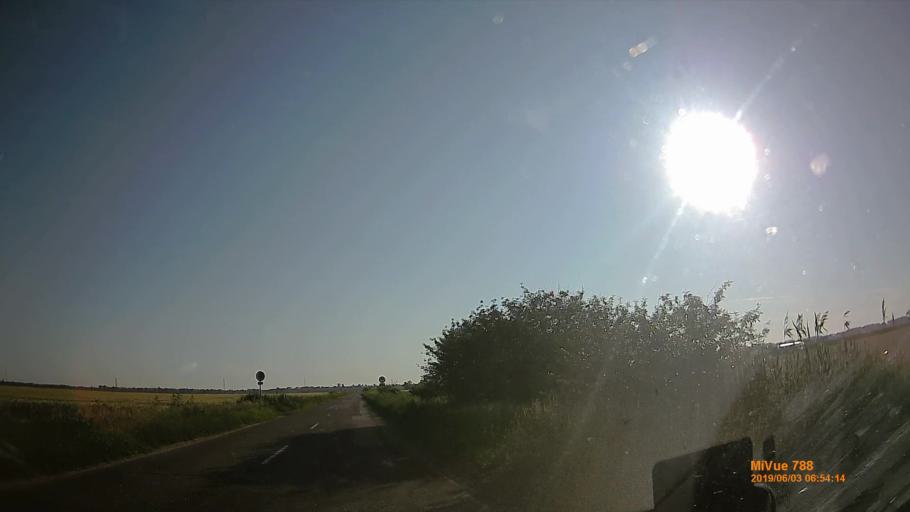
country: HU
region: Pest
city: Bugyi
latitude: 47.2127
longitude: 19.2236
